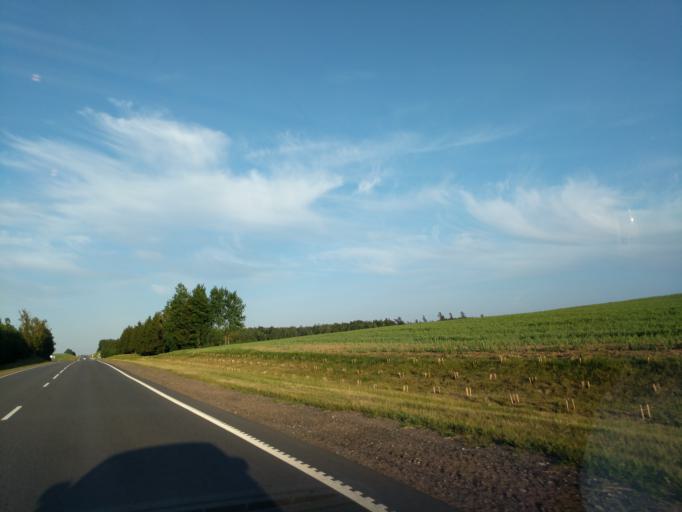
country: BY
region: Minsk
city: Bal'shavik
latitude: 54.0947
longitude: 27.5099
